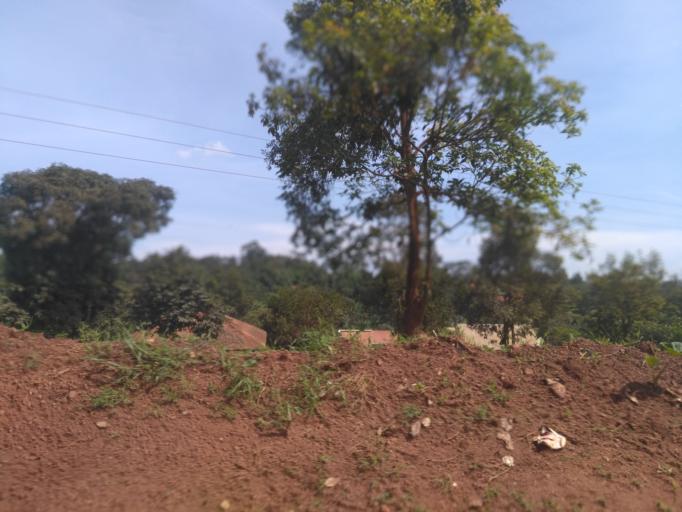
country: UG
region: Central Region
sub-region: Wakiso District
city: Kireka
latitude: 0.4418
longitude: 32.5875
